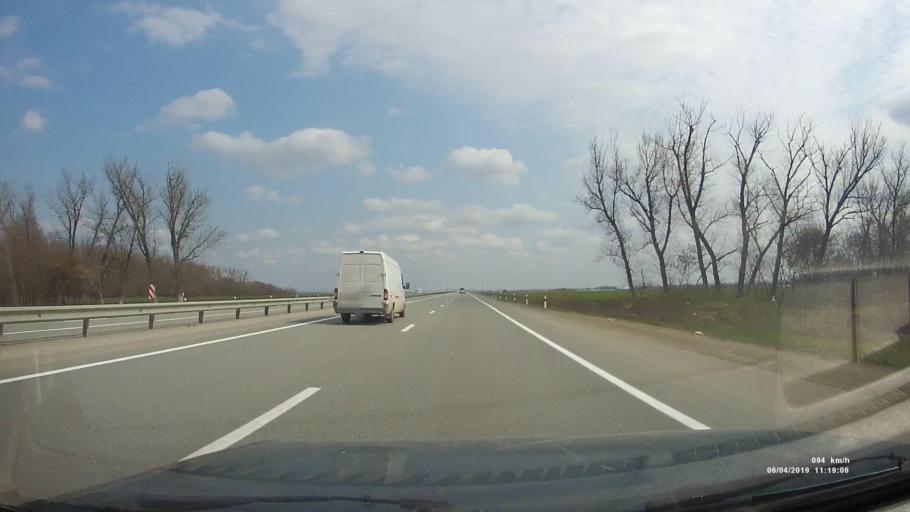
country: RU
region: Rostov
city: Kuleshovka
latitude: 47.1026
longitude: 39.6154
